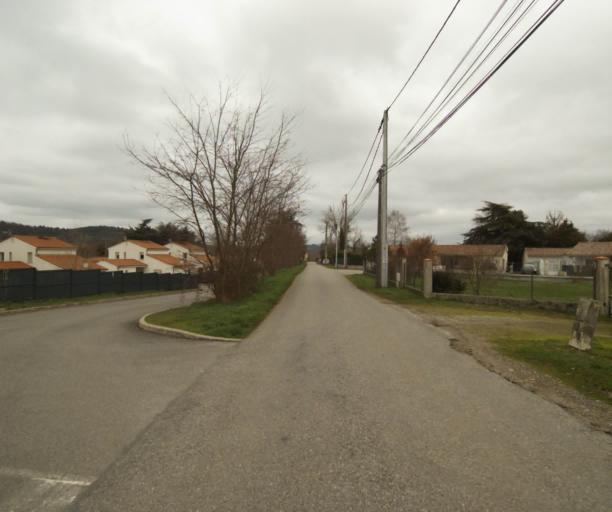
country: FR
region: Midi-Pyrenees
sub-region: Departement de l'Ariege
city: Pamiers
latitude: 43.1349
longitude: 1.6025
